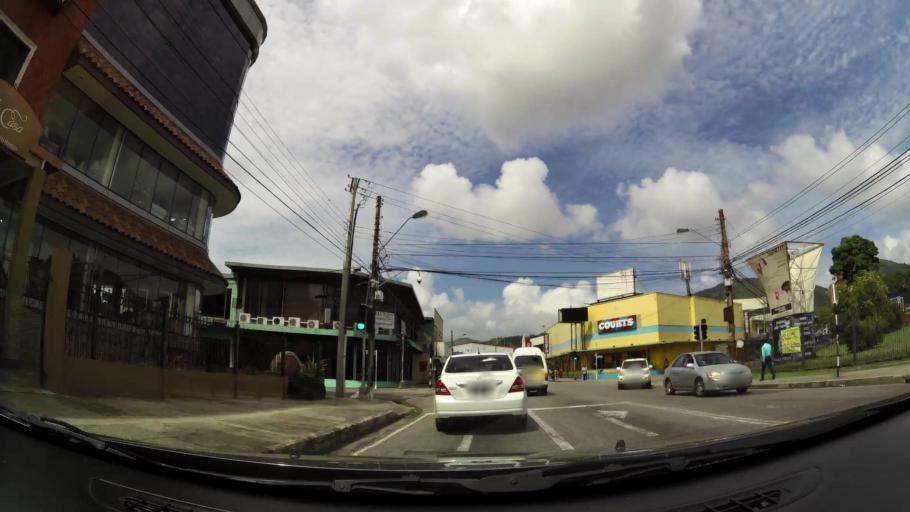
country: TT
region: City of Port of Spain
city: Mucurapo
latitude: 10.6704
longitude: -61.5293
